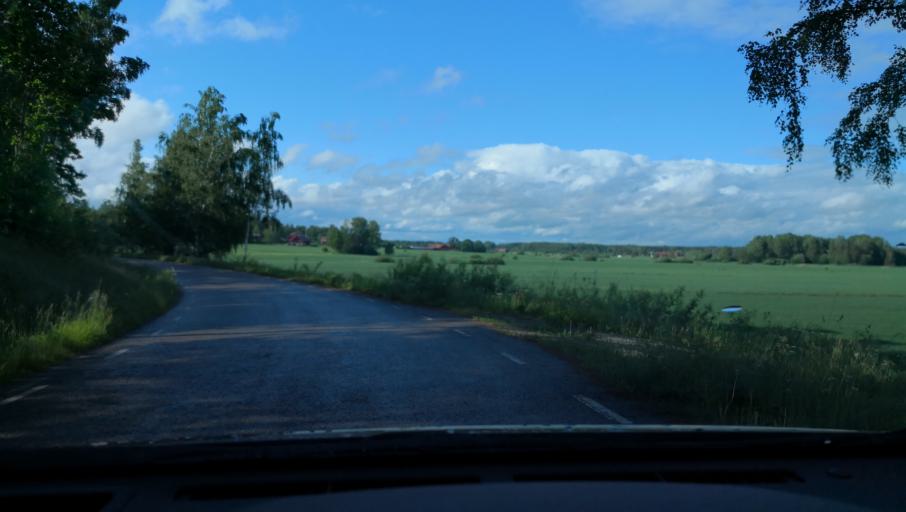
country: SE
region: OErebro
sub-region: Lindesbergs Kommun
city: Fellingsbro
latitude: 59.3080
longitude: 15.6804
